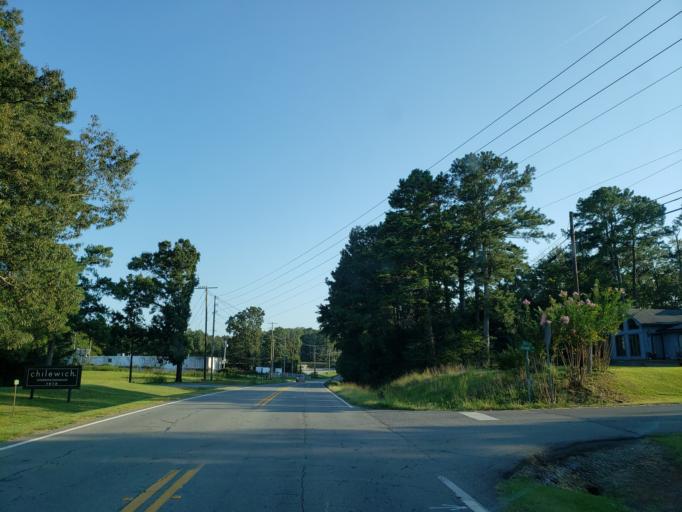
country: US
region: Georgia
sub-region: Murray County
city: Chatsworth
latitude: 34.7407
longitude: -84.8200
